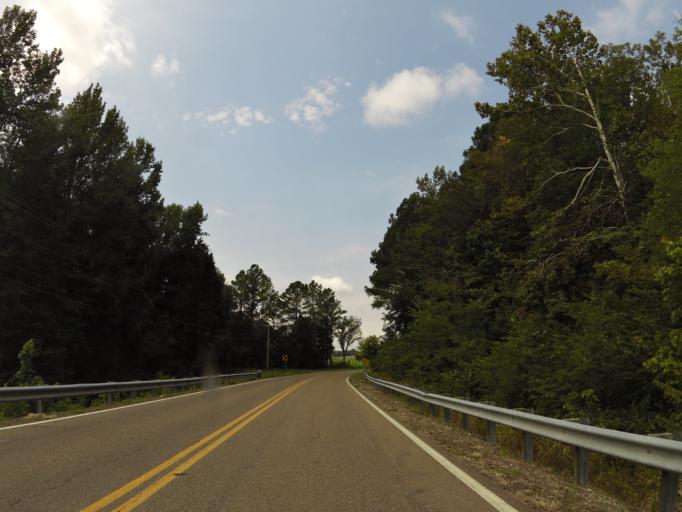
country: US
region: Tennessee
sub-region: Decatur County
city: Decaturville
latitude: 35.5797
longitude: -88.0961
